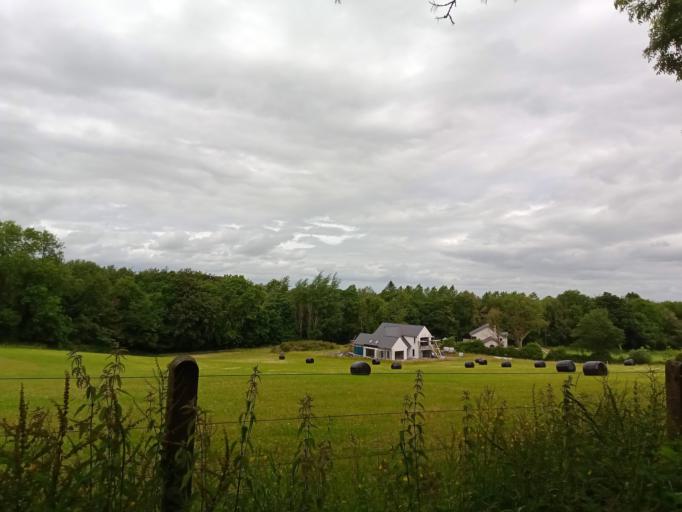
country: IE
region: Leinster
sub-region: Kilkenny
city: Piltown
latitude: 52.4599
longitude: -7.2729
